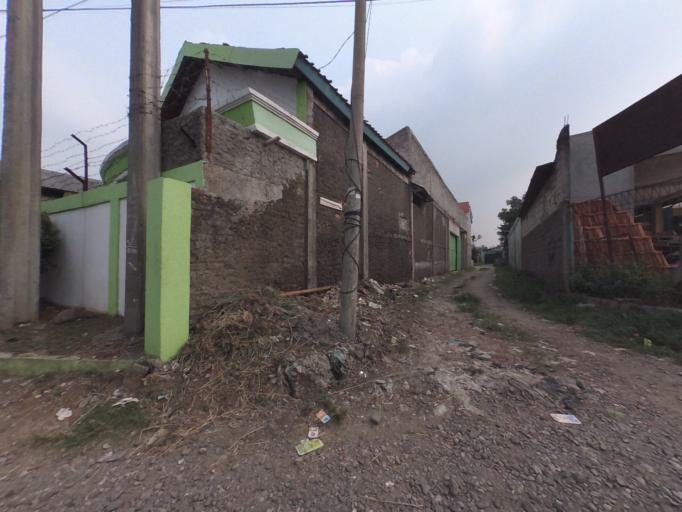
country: ID
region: West Java
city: Ciampea
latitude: -6.5644
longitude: 106.6766
